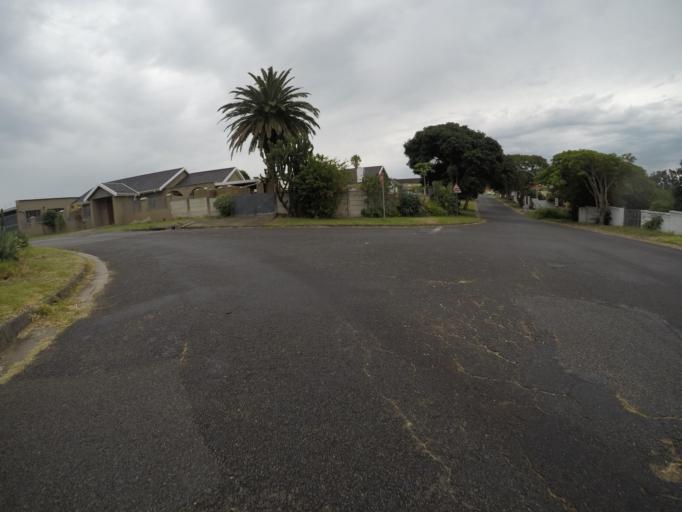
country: ZA
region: Eastern Cape
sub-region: Buffalo City Metropolitan Municipality
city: East London
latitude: -32.9933
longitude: 27.8503
